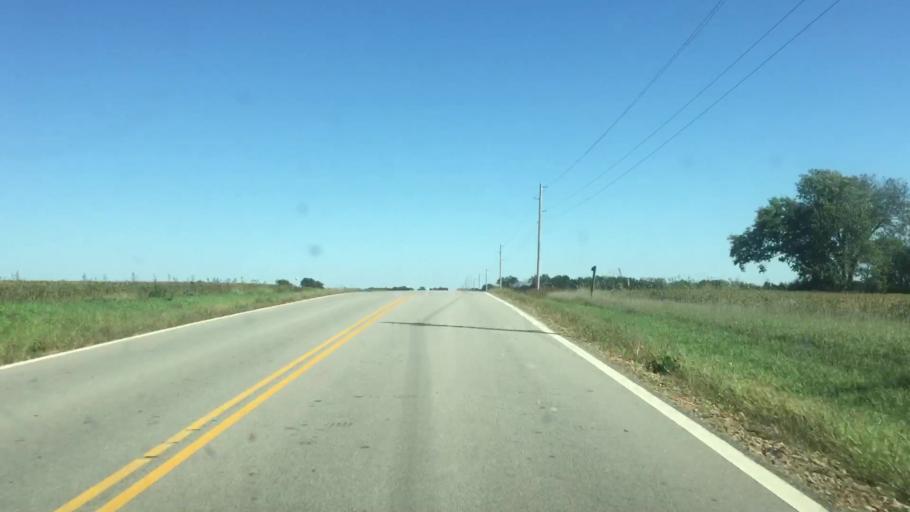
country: US
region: Kansas
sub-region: Jackson County
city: Holton
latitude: 39.5949
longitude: -95.6916
